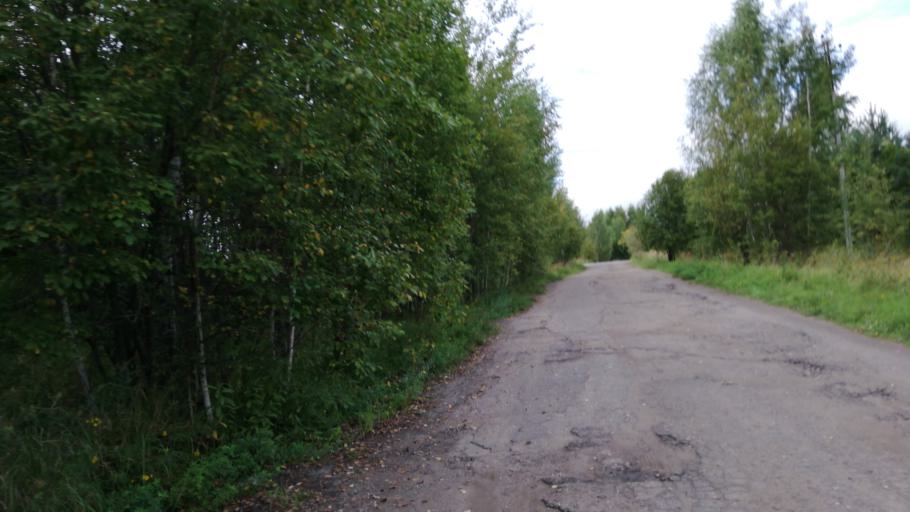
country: RU
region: Jaroslavl
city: Konstantinovskiy
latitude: 57.8020
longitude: 39.7176
